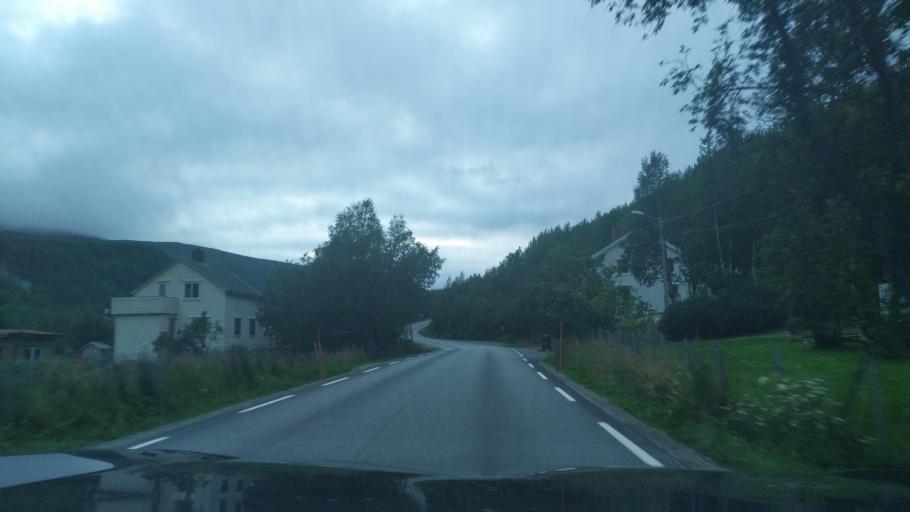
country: NO
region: Troms
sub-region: Lavangen
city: Tennevoll
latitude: 68.7245
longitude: 17.8386
